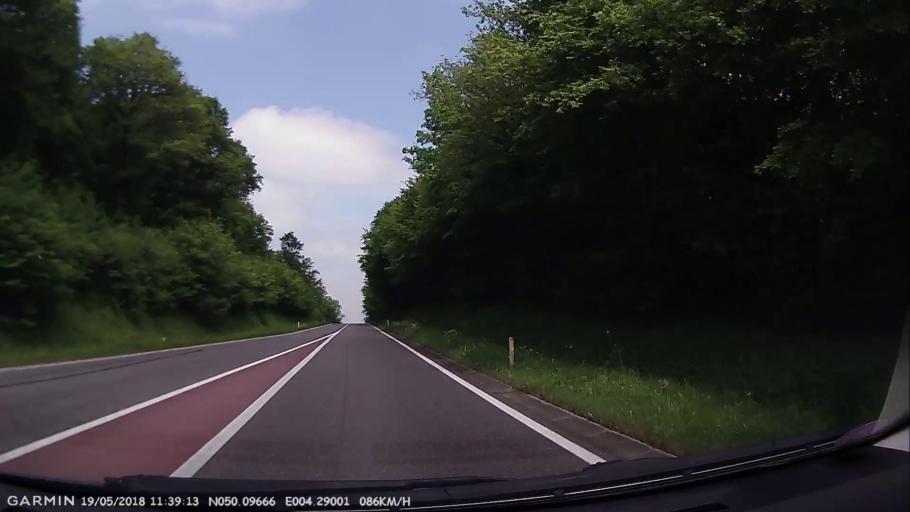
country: BE
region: Wallonia
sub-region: Province du Hainaut
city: Chimay
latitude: 50.0969
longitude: 4.2899
